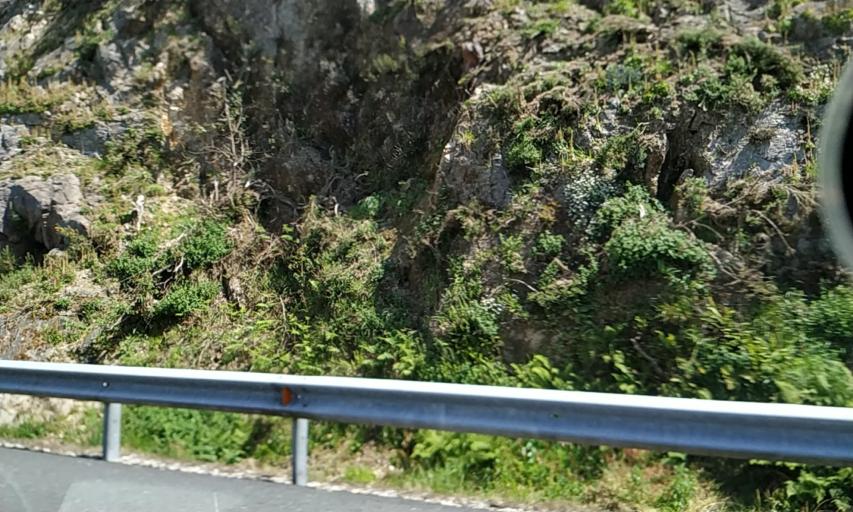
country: ES
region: Galicia
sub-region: Provincia da Coruna
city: Santiago de Compostela
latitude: 42.8384
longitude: -8.5716
